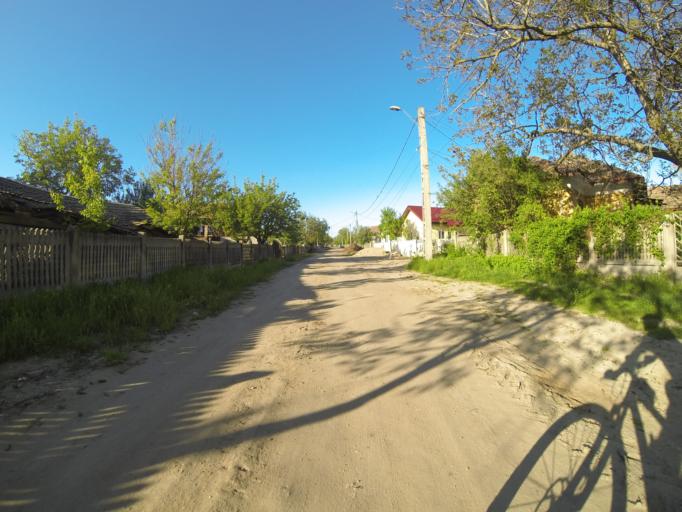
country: RO
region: Dolj
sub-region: Comuna Segarcea
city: Segarcea
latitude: 44.0925
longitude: 23.7358
